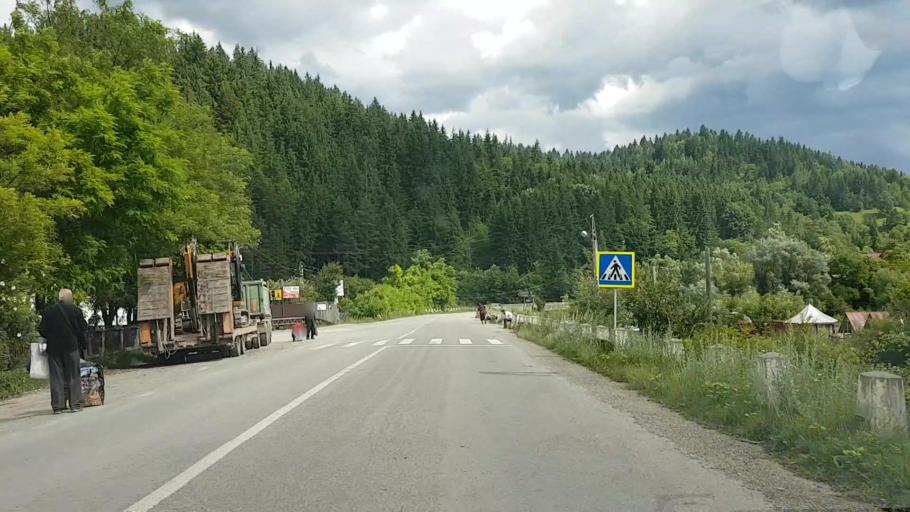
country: RO
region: Neamt
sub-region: Comuna Hangu
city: Hangu
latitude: 47.0600
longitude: 26.0353
